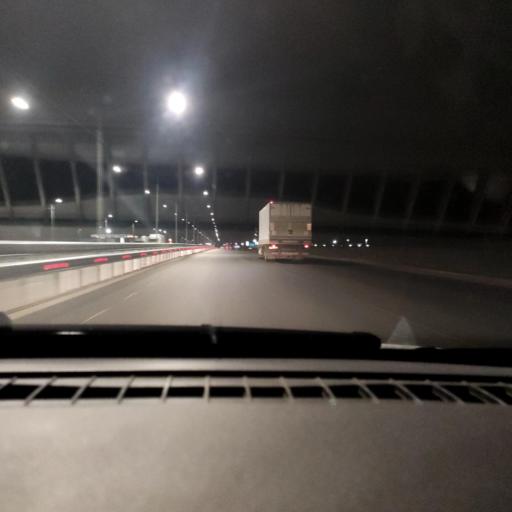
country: RU
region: Lipetsk
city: Khlevnoye
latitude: 52.0412
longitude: 39.1978
